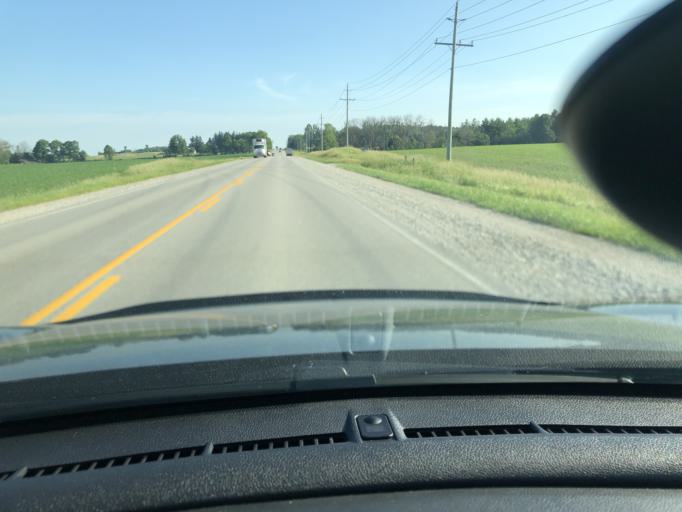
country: CA
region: Ontario
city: Stratford
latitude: 43.3925
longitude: -80.8373
